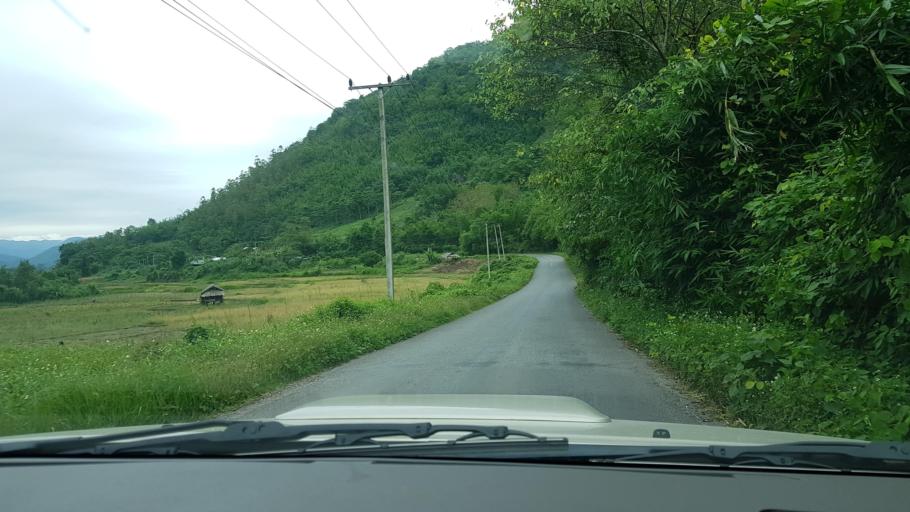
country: LA
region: Oudomxai
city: Muang La
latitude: 20.8209
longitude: 102.0947
